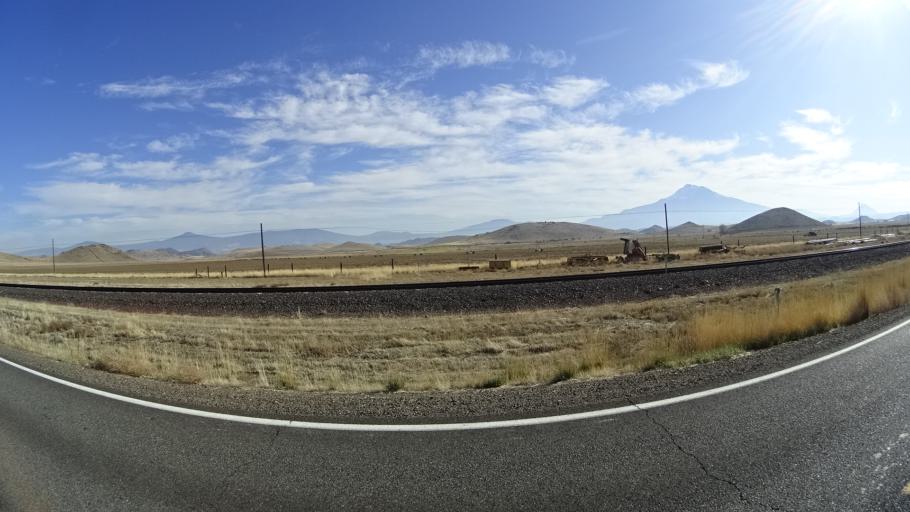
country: US
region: California
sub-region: Siskiyou County
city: Montague
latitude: 41.5468
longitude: -122.5260
